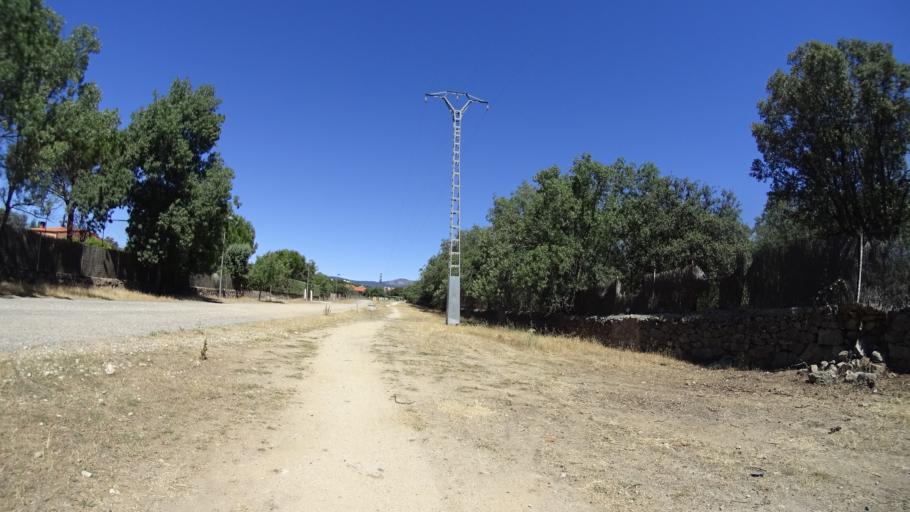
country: ES
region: Madrid
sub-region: Provincia de Madrid
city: Alpedrete
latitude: 40.6493
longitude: -4.0395
